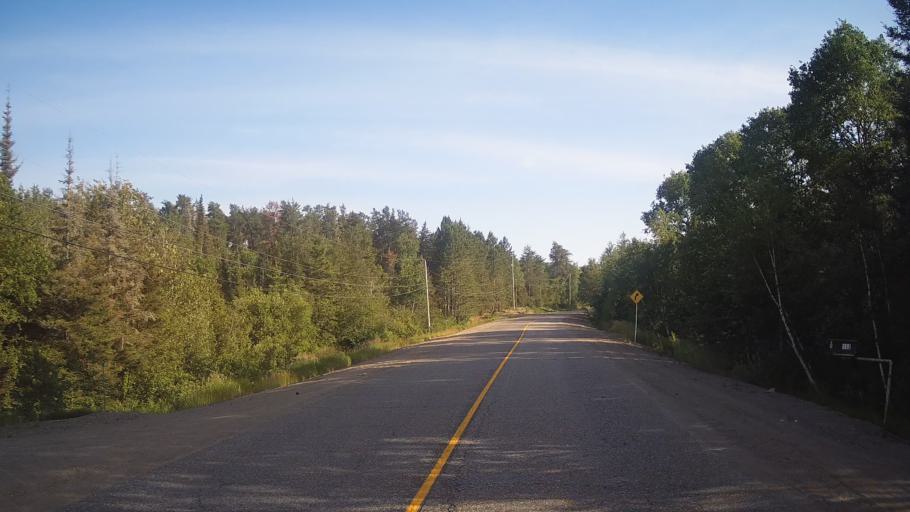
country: CA
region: Ontario
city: Rayside-Balfour
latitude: 46.5757
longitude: -81.3084
